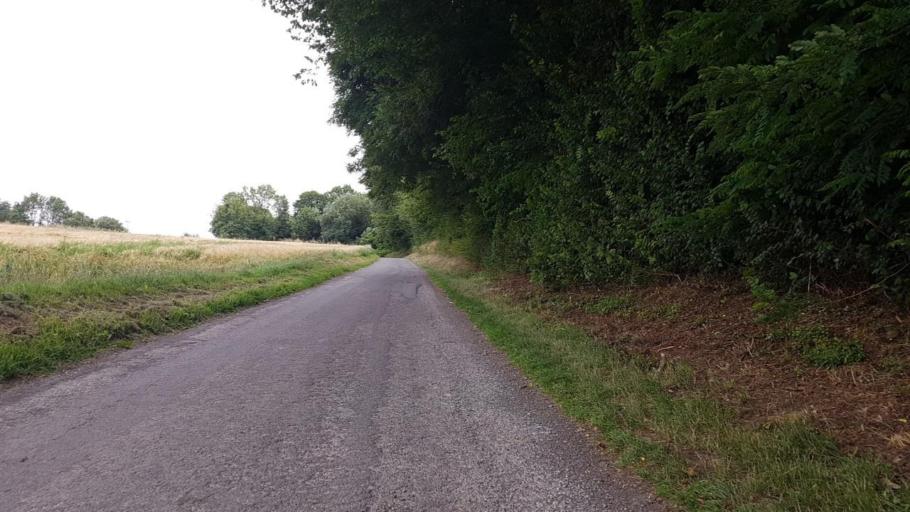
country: FR
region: Picardie
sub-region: Departement de l'Aisne
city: Guise
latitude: 49.8957
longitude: 3.6194
